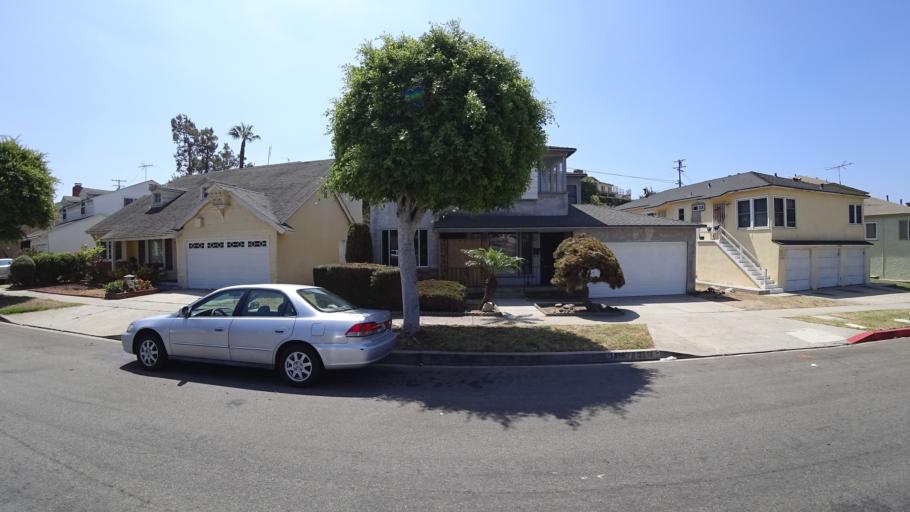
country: US
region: California
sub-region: Los Angeles County
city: Westmont
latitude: 33.9444
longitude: -118.3251
